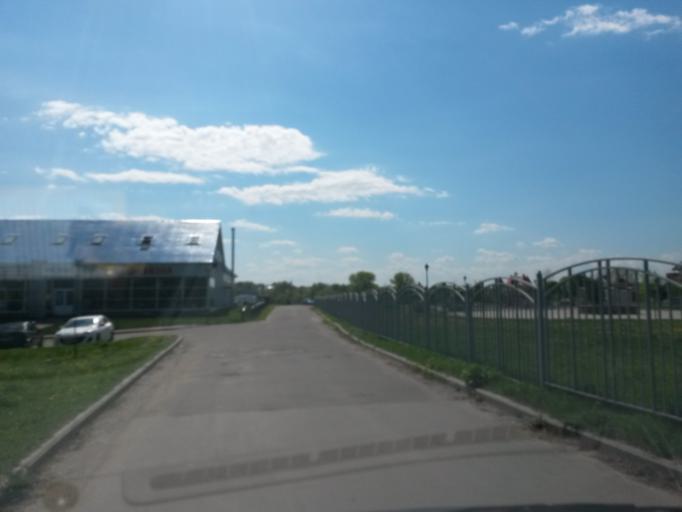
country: RU
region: Jaroslavl
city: Yaroslavl
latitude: 57.6182
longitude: 39.8730
